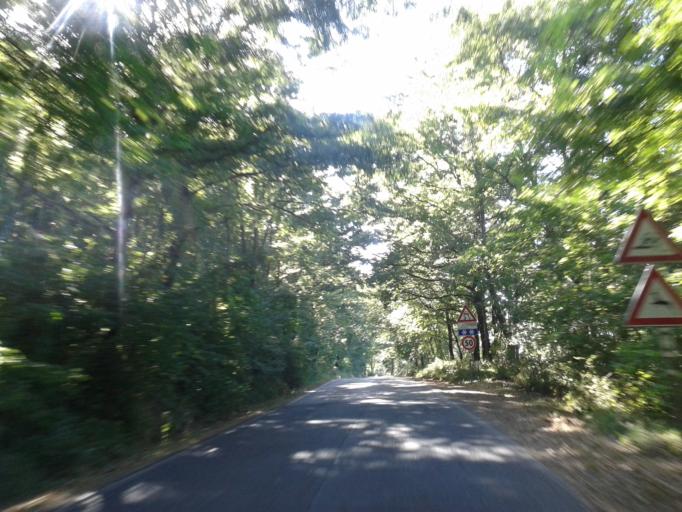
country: IT
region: Tuscany
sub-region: Province of Pisa
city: Castellina Marittima
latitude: 43.4200
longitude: 10.5980
